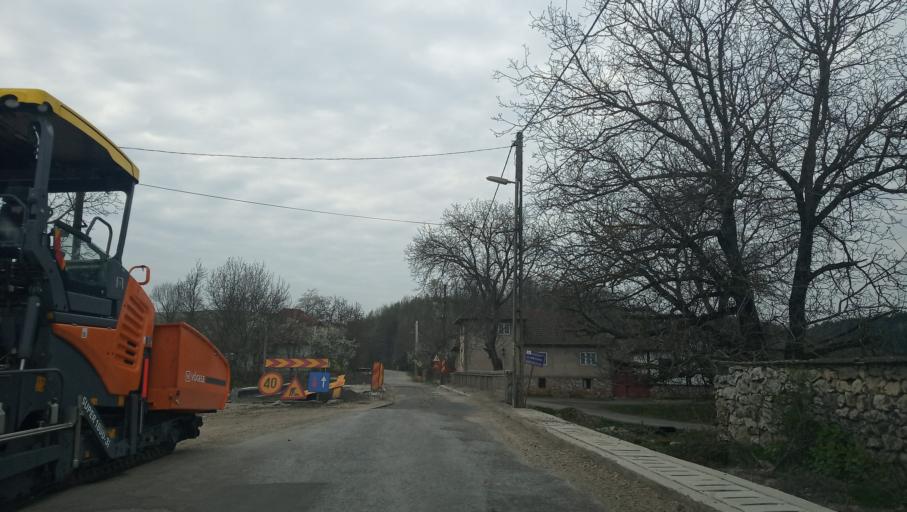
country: RO
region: Bihor
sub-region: Comuna Carpinet
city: Carpinet
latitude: 46.4538
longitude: 22.4949
